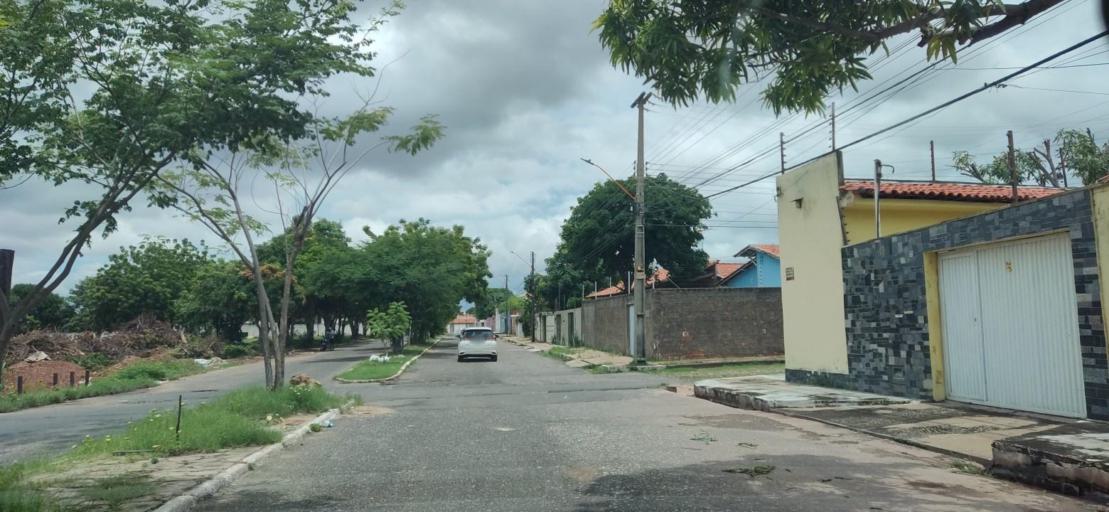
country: BR
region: Piaui
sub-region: Teresina
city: Teresina
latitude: -5.0744
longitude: -42.7543
